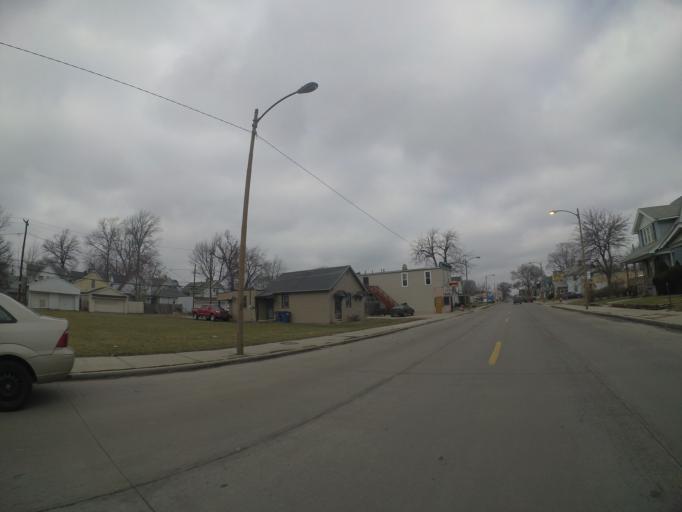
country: US
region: Ohio
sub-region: Lucas County
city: Oregon
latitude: 41.6375
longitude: -83.5157
